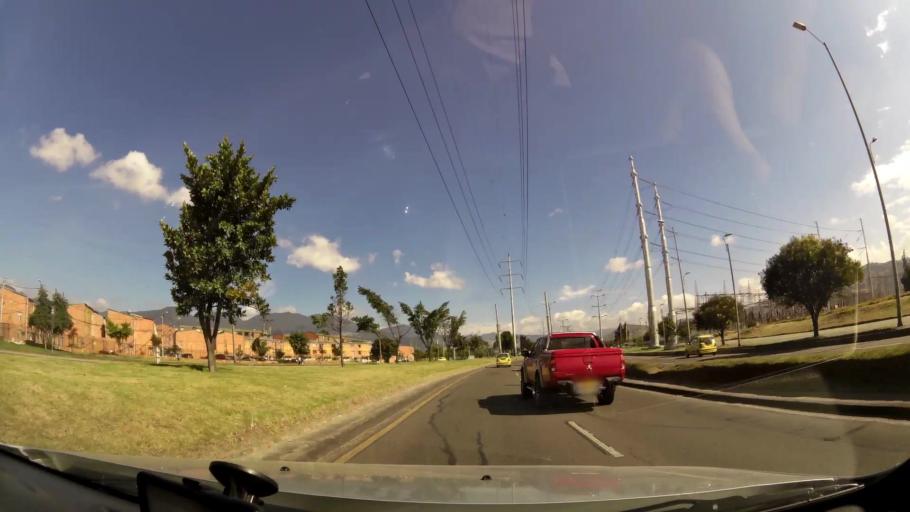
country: CO
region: Bogota D.C.
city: Bogota
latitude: 4.5759
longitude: -74.1404
